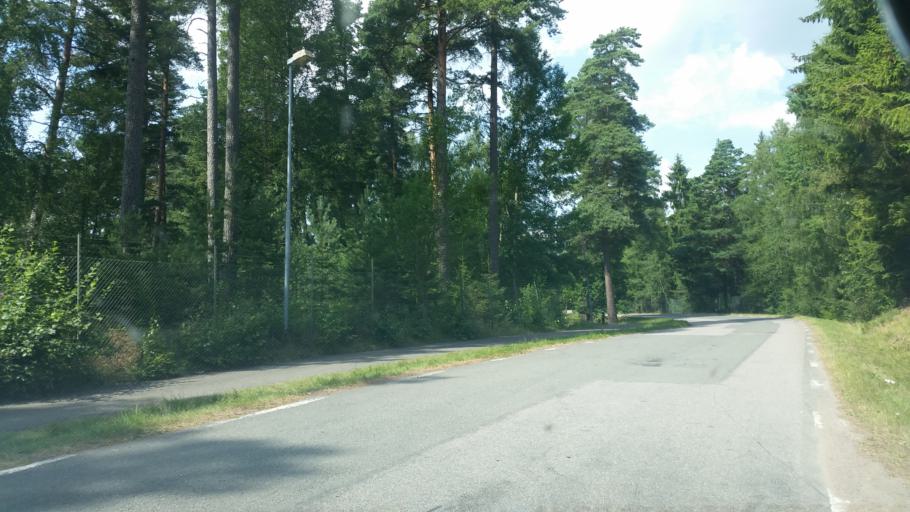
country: SE
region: Vaestra Goetaland
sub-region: Skara Kommun
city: Axvall
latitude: 58.4117
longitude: 13.5529
